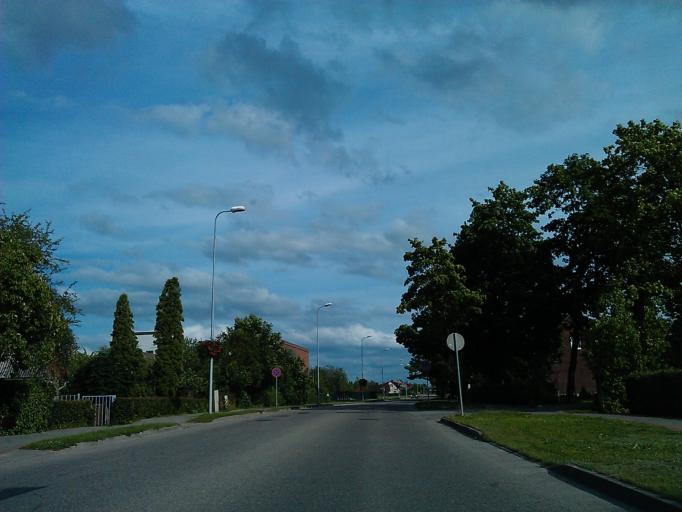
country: LV
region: Cesu Rajons
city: Cesis
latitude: 57.3066
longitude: 25.2850
